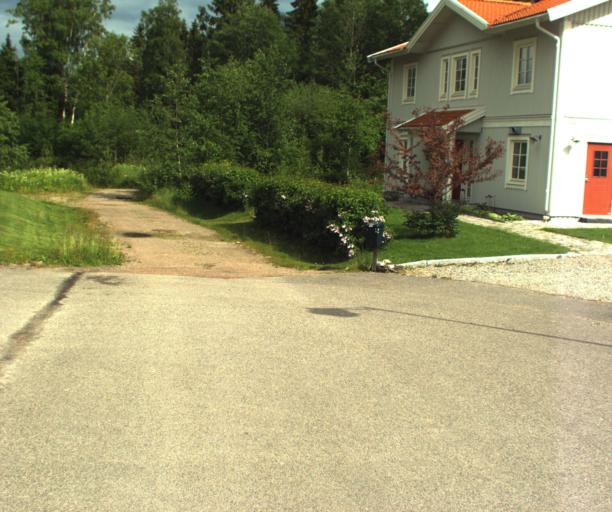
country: SE
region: Gaevleborg
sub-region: Gavle Kommun
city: Valbo
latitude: 60.6767
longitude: 17.0746
